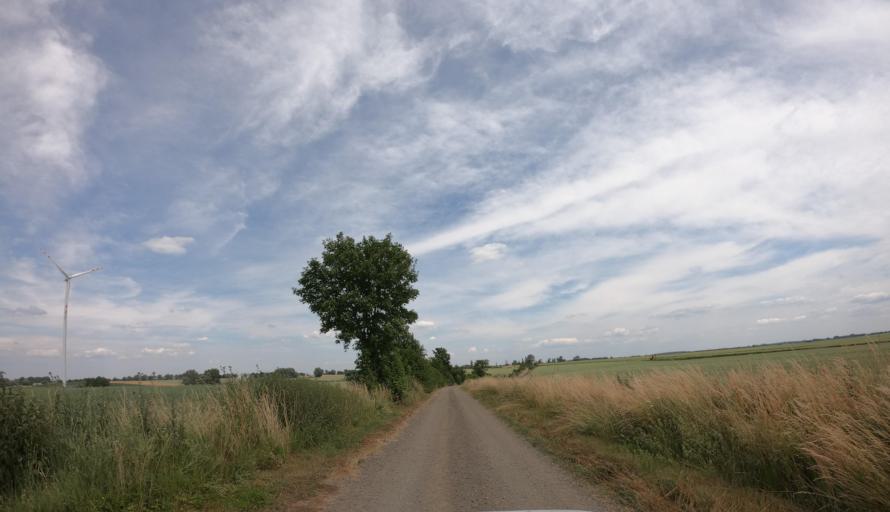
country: PL
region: West Pomeranian Voivodeship
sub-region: Powiat pyrzycki
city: Kozielice
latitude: 53.1216
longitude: 14.8363
